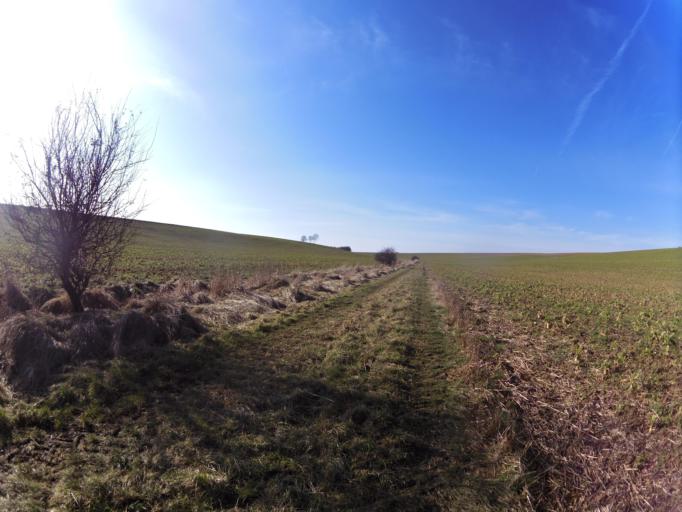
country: DE
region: Bavaria
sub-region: Regierungsbezirk Unterfranken
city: Winterhausen
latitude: 49.6798
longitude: 9.9846
